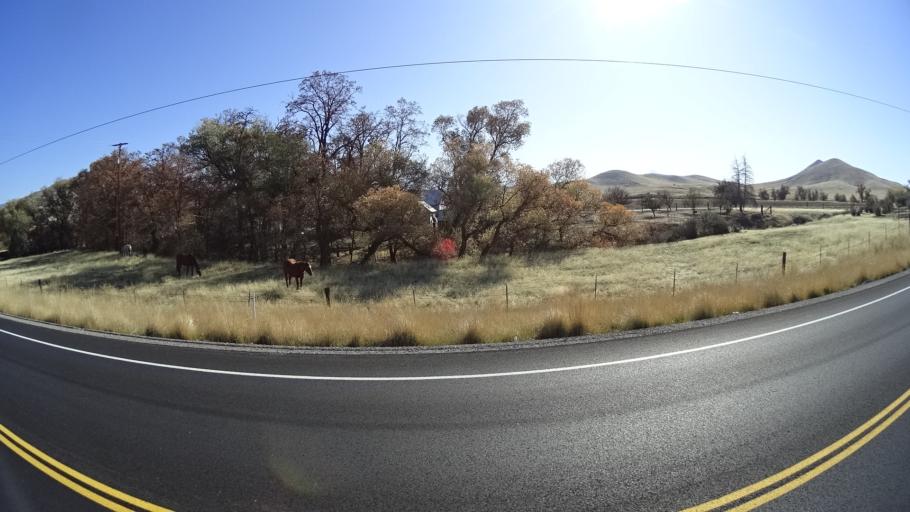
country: US
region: California
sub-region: Siskiyou County
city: Montague
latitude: 41.8451
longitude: -122.4741
